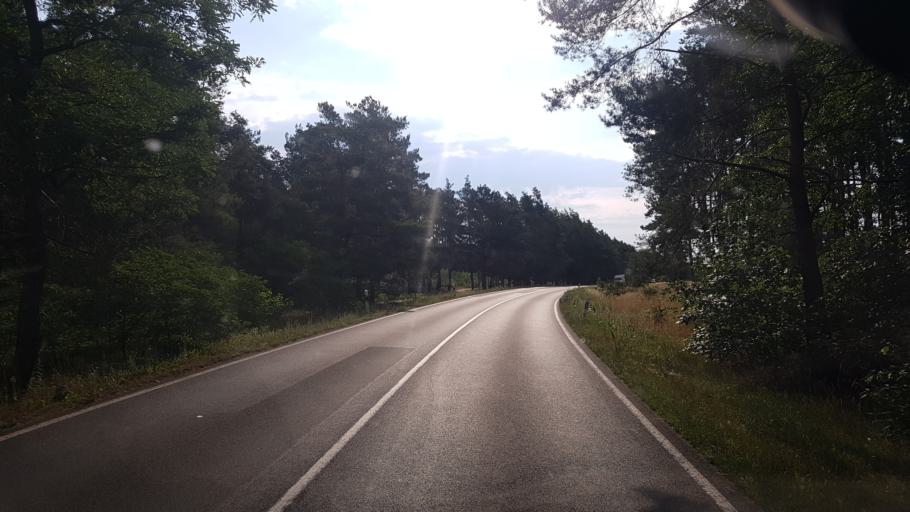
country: DE
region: Brandenburg
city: Baruth
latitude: 52.0581
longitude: 13.5549
